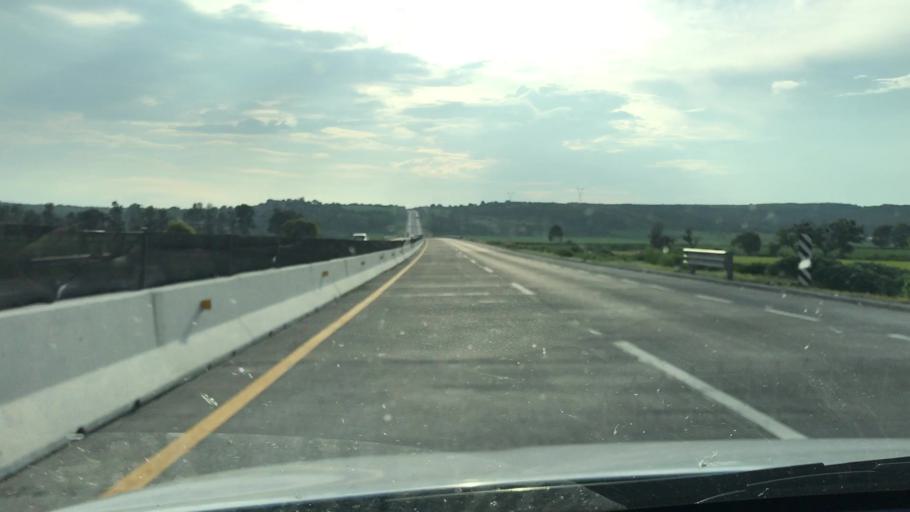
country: MX
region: Guanajuato
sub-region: Penjamo
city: Estacion la Piedad
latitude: 20.3994
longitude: -102.0071
